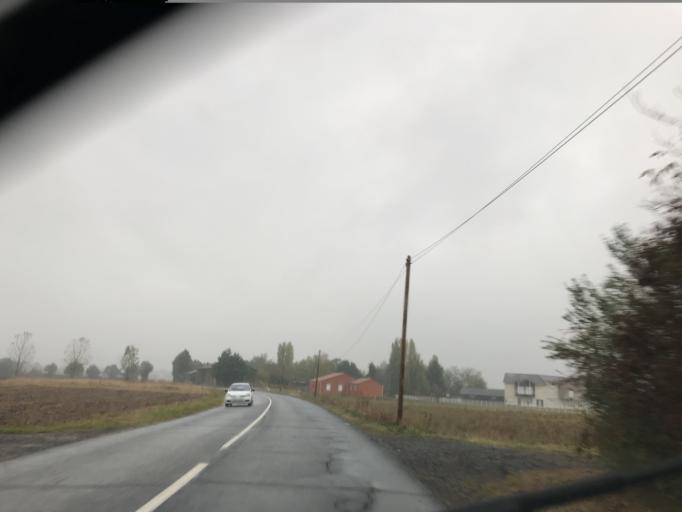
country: FR
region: Auvergne
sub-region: Departement du Puy-de-Dome
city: Vertaizon
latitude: 45.7810
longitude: 3.3269
